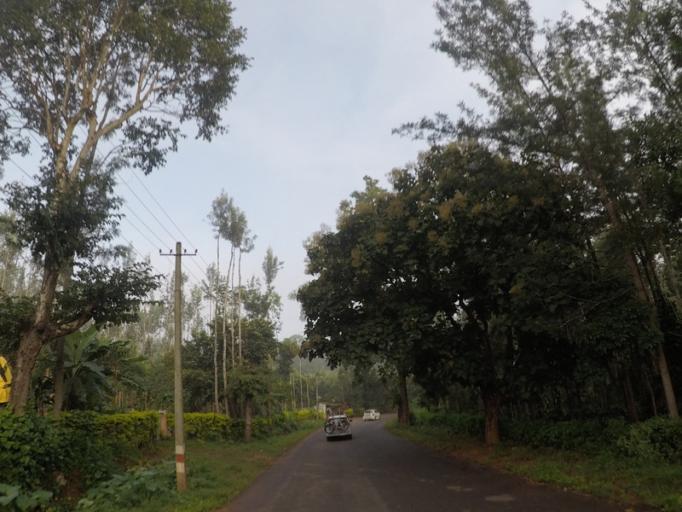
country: IN
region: Karnataka
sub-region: Chikmagalur
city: Chikmagalur
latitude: 13.4346
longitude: 75.8081
